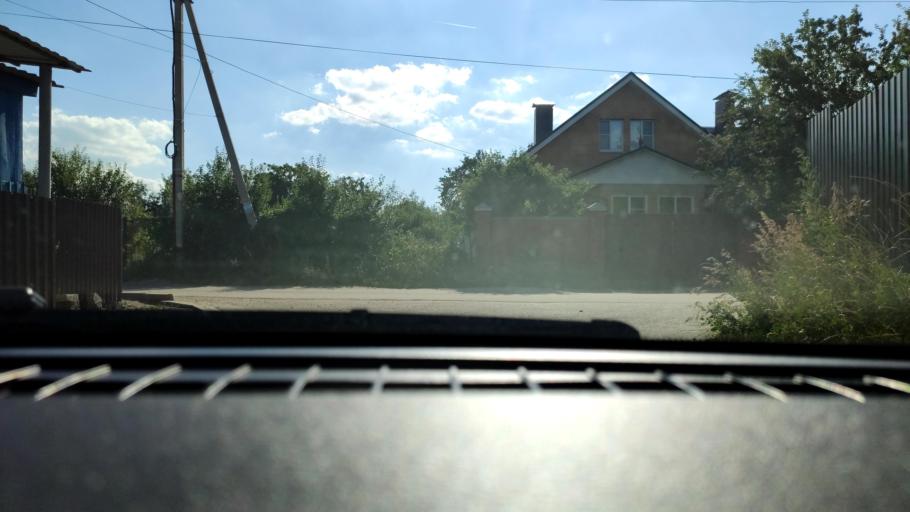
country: RU
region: Voronezj
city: Ramon'
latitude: 51.8143
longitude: 39.2677
